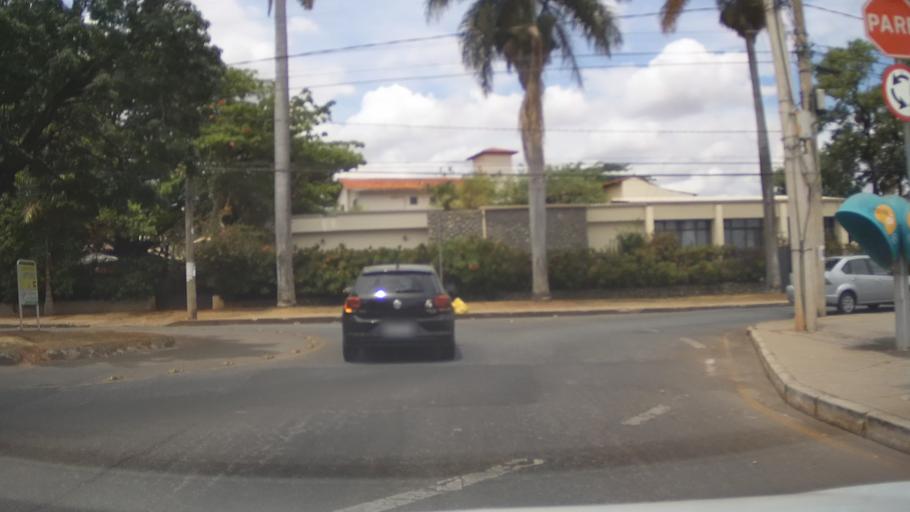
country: BR
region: Minas Gerais
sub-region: Belo Horizonte
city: Belo Horizonte
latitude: -19.8607
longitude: -43.9716
